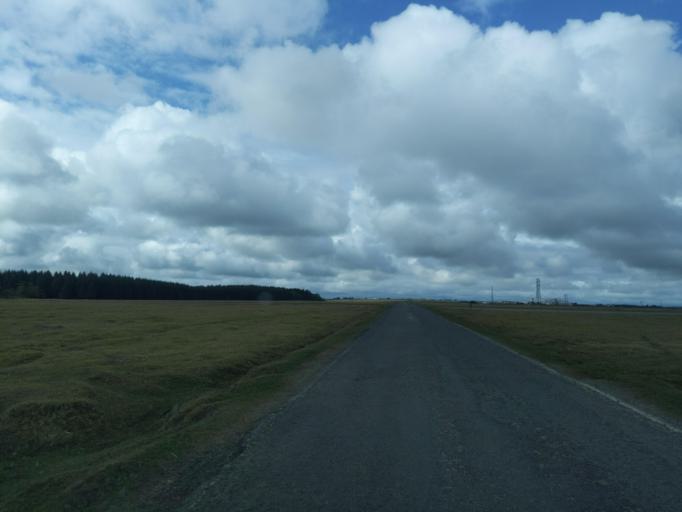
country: GB
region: England
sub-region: Cornwall
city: Camelford
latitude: 50.6344
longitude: -4.6149
